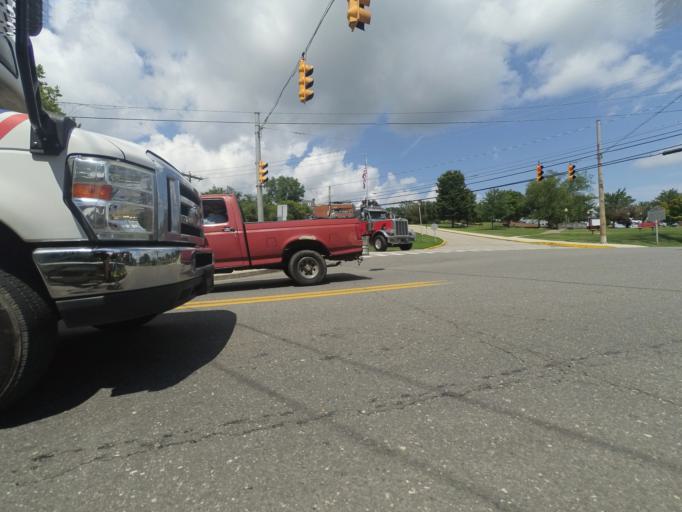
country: US
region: West Virginia
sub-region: Cabell County
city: Barboursville
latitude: 38.4102
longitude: -82.2958
